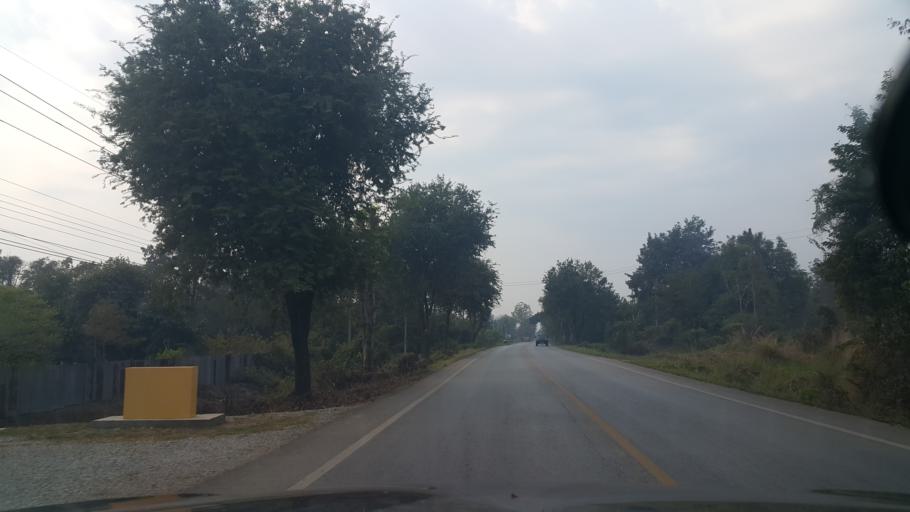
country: TH
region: Sukhothai
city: Si Samrong
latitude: 17.1063
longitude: 99.8887
